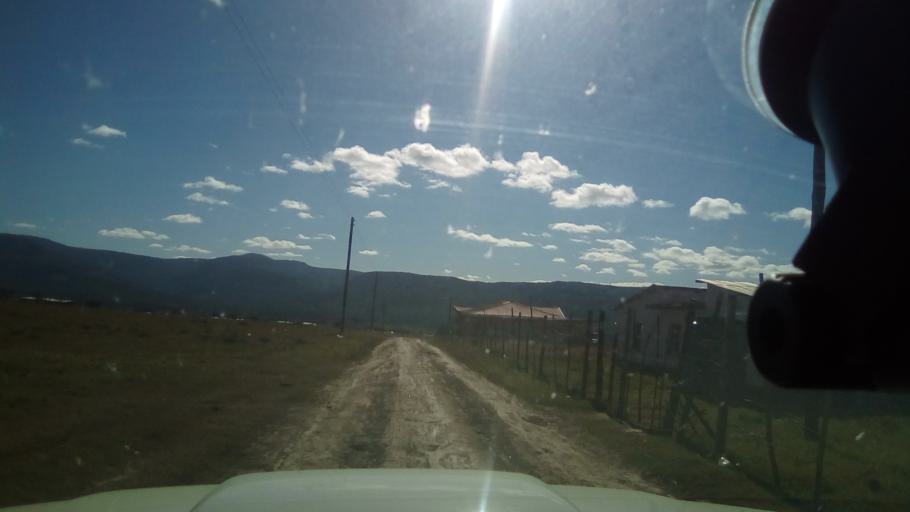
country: ZA
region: Eastern Cape
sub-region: Buffalo City Metropolitan Municipality
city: Bhisho
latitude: -32.7834
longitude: 27.3323
